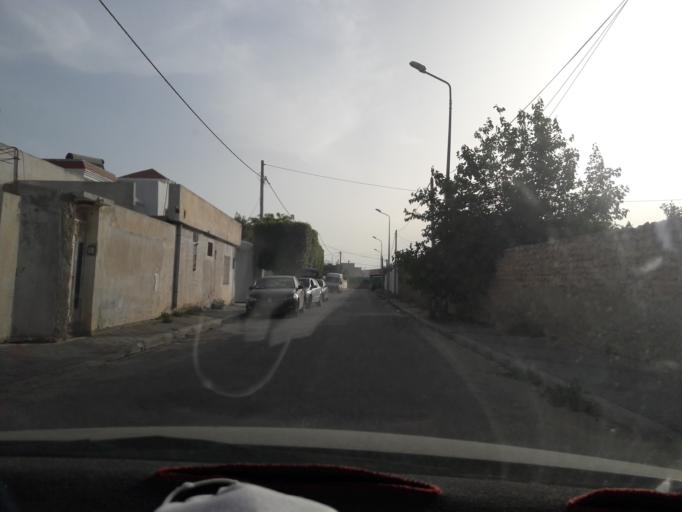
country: TN
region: Safaqis
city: Al Qarmadah
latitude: 34.8007
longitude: 10.7549
